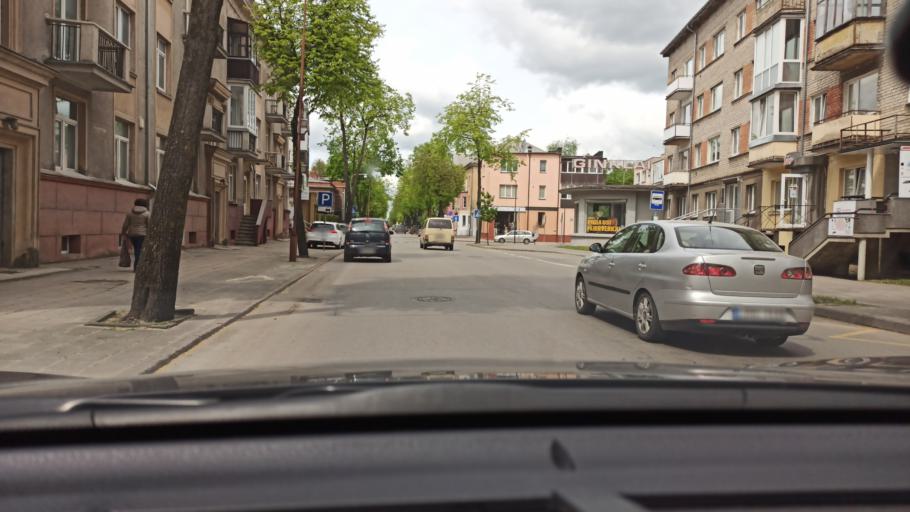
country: LT
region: Siauliu apskritis
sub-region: Siauliai
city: Siauliai
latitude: 55.9303
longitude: 23.3095
